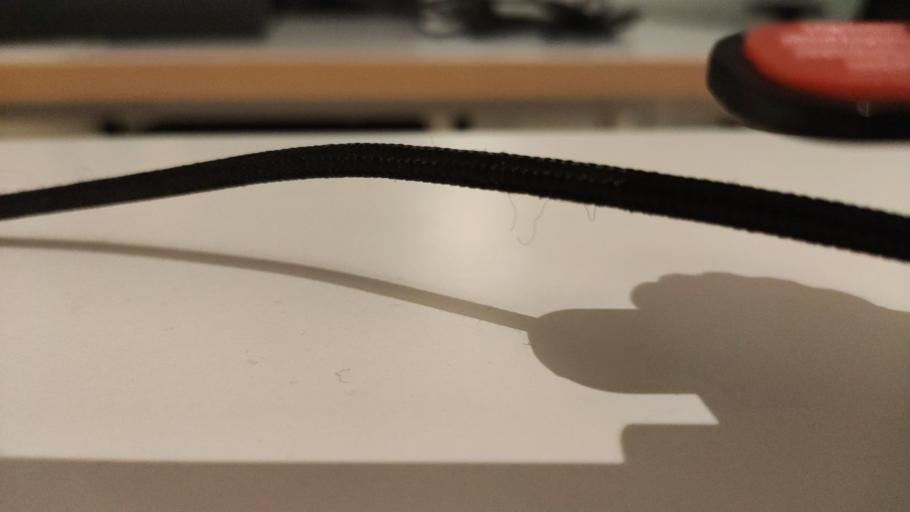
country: RU
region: Moskovskaya
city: Shemetovo
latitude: 56.4140
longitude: 37.9918
